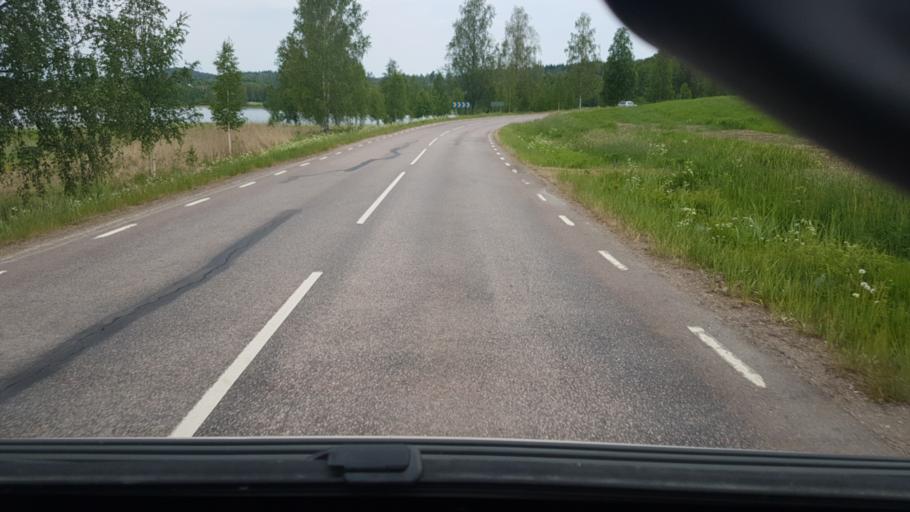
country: SE
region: Vaermland
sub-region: Arvika Kommun
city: Arvika
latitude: 59.7844
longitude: 12.6205
